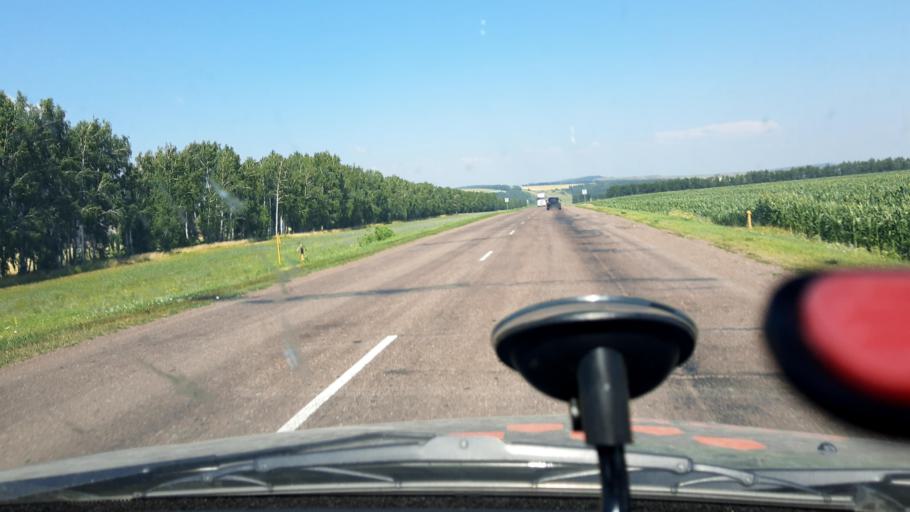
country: RU
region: Bashkortostan
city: Chekmagush
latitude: 55.1205
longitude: 54.6683
